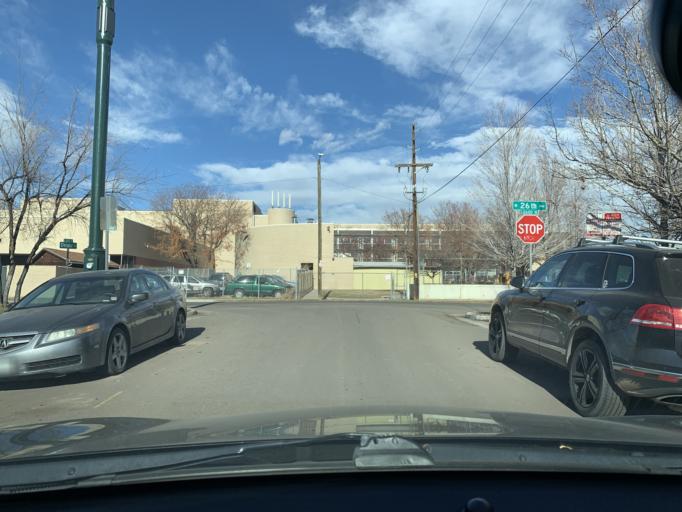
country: US
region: Colorado
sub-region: Denver County
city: Denver
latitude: 39.7546
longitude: -105.0221
